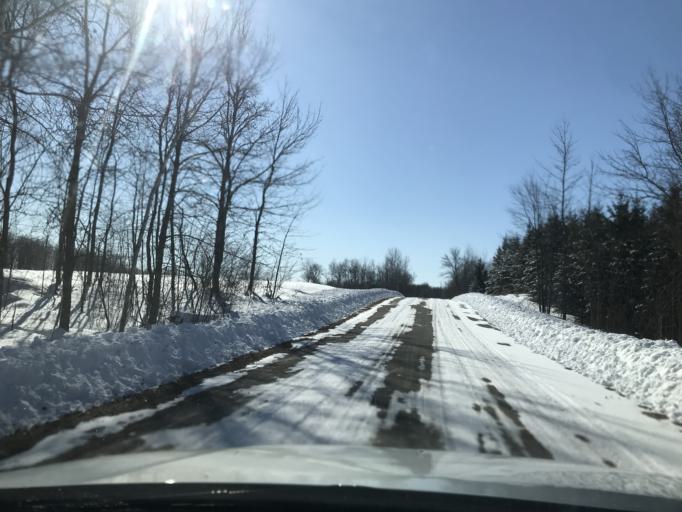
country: US
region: Wisconsin
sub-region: Marinette County
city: Peshtigo
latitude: 45.1738
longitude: -87.7640
